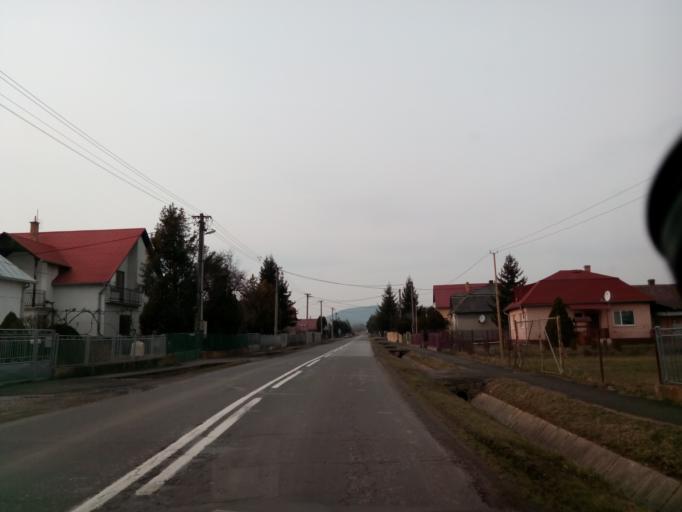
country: SK
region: Kosicky
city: Secovce
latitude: 48.6146
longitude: 21.6029
